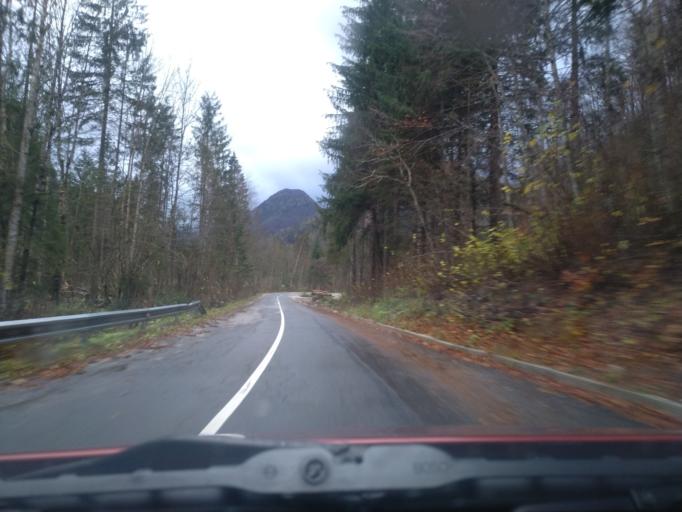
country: SI
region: Solcava
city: Solcava
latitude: 46.4214
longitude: 14.6488
